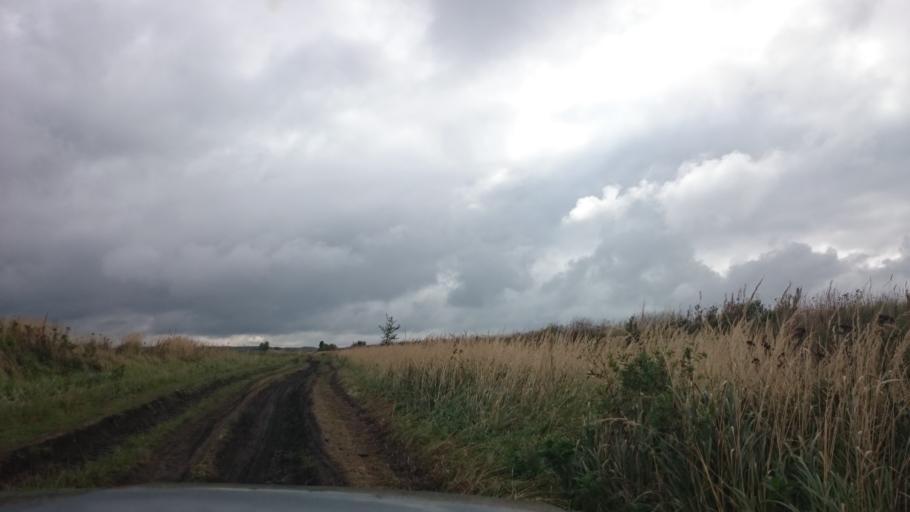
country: RU
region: Mordoviya
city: Kadoshkino
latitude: 54.0156
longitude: 44.4647
